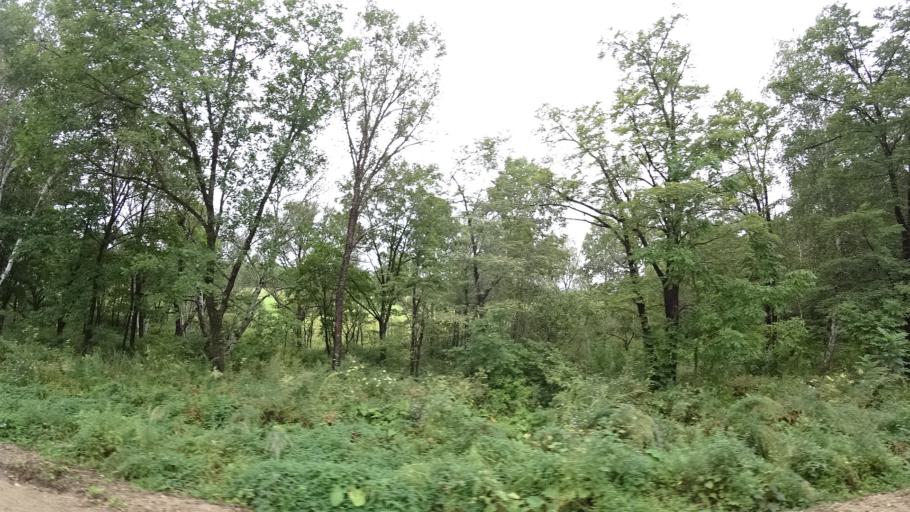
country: RU
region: Primorskiy
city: Rettikhovka
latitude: 44.0649
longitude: 132.6509
